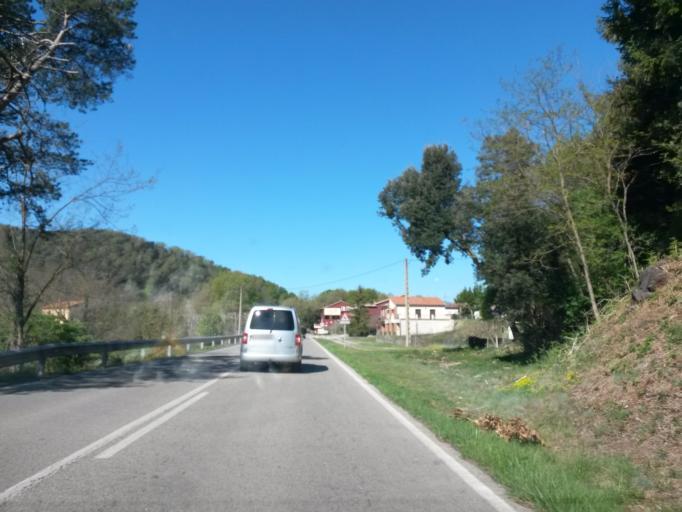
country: ES
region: Catalonia
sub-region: Provincia de Girona
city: Santa Pau
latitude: 42.1484
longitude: 2.5334
